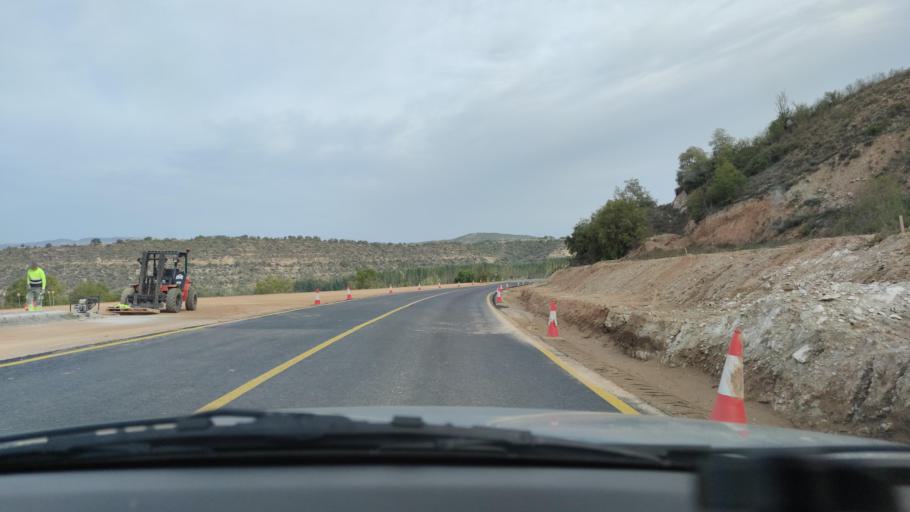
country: ES
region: Catalonia
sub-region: Provincia de Lleida
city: Artesa de Segre
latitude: 41.8983
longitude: 1.0601
